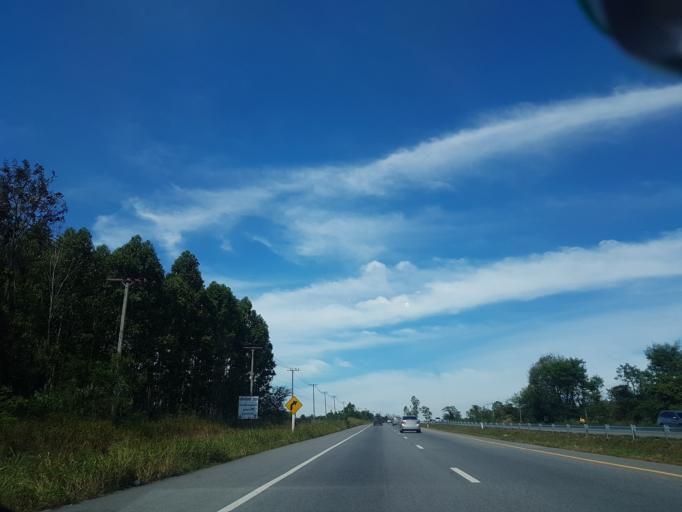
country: TH
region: Chon Buri
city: Phatthaya
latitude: 12.8788
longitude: 101.0232
